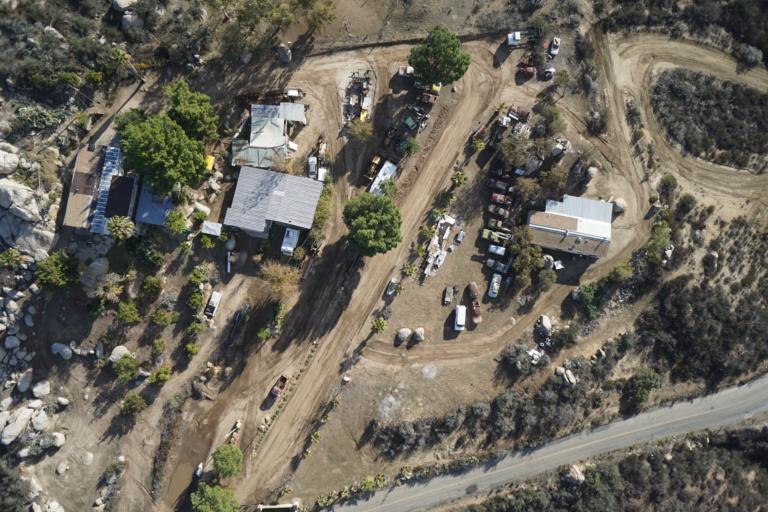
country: US
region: California
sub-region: Riverside County
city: East Hemet
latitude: 33.6357
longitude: -116.9127
